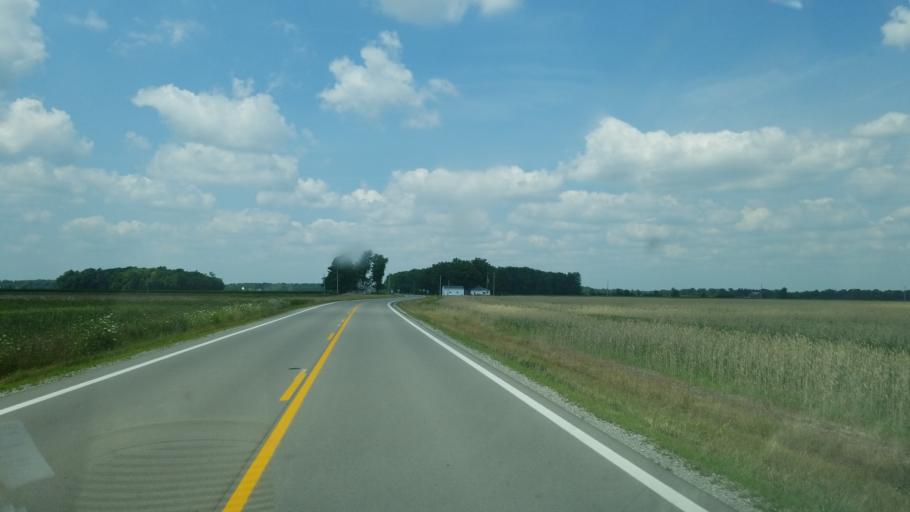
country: US
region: Ohio
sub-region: Henry County
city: Holgate
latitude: 41.2821
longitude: -84.2235
